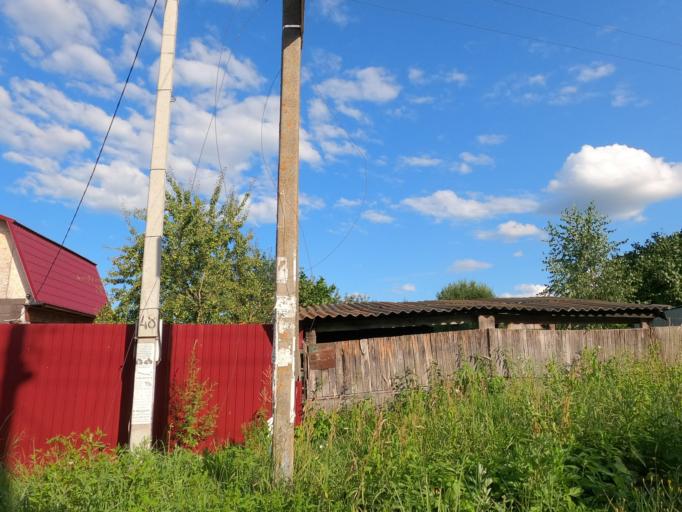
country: RU
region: Moskovskaya
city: Konobeyevo
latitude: 55.4122
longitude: 38.7197
